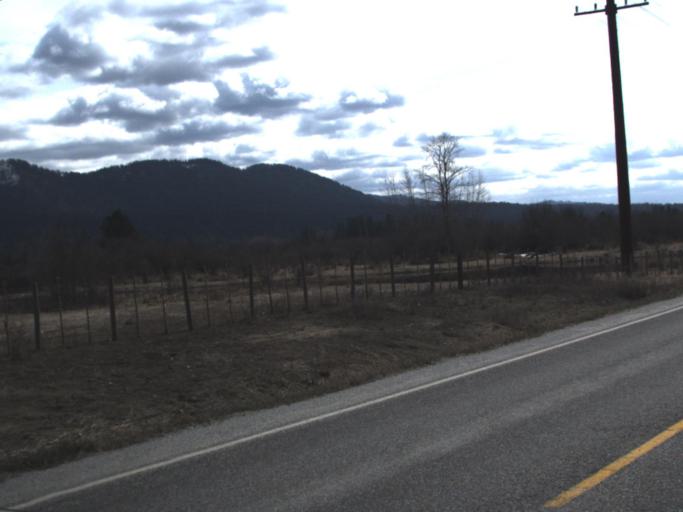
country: US
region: Washington
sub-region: Pend Oreille County
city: Newport
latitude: 48.3816
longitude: -117.3087
